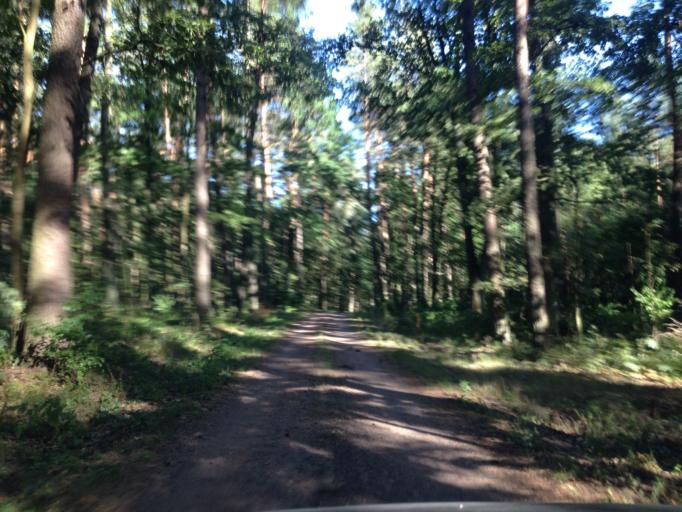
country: PL
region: Kujawsko-Pomorskie
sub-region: Powiat brodnicki
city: Gorzno
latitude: 53.1598
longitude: 19.6244
